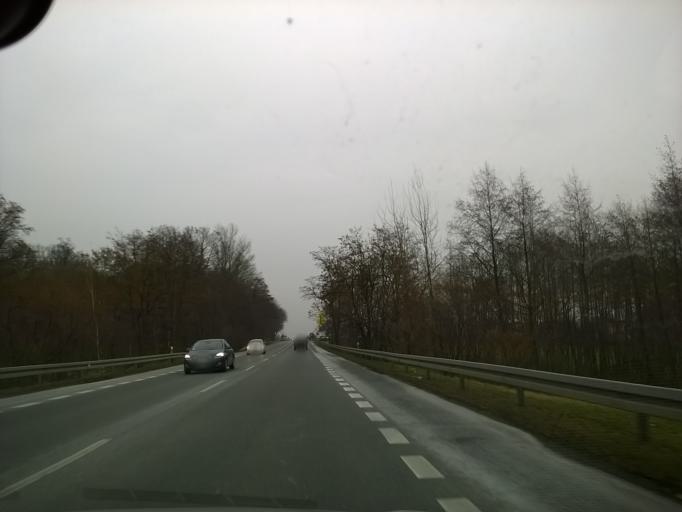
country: PL
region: Silesian Voivodeship
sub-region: Powiat gliwicki
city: Przyszowice
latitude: 50.2441
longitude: 18.7560
